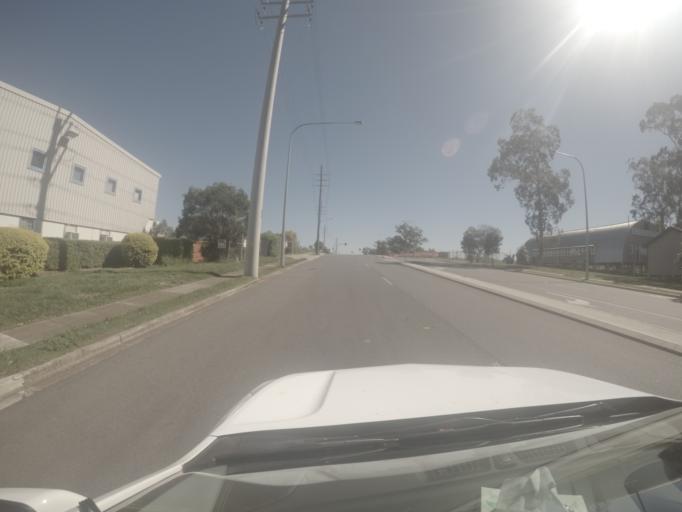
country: AU
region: Queensland
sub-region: Brisbane
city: Wacol
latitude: -27.5839
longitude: 152.9432
